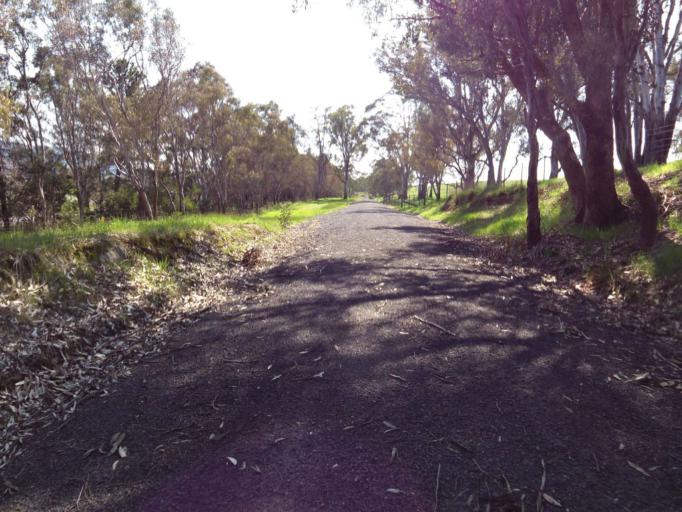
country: AU
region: Victoria
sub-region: Murrindindi
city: Alexandra
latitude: -37.1357
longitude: 145.5920
